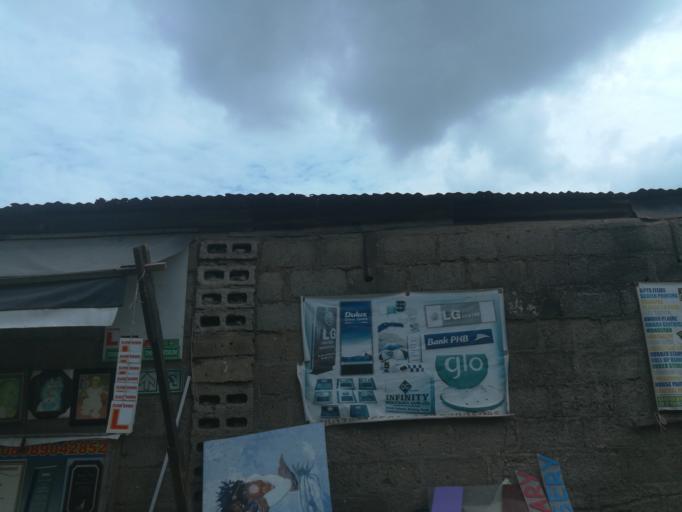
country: NG
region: Lagos
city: Somolu
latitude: 6.5475
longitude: 3.3921
